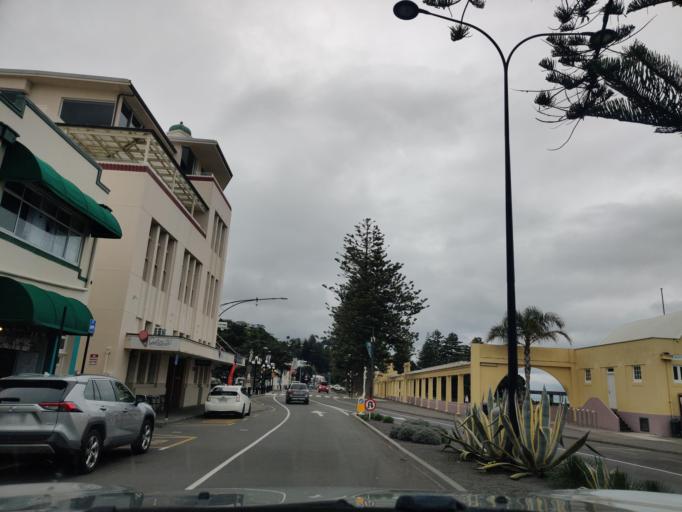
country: NZ
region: Hawke's Bay
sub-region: Napier City
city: Napier
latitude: -39.4905
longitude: 176.9193
